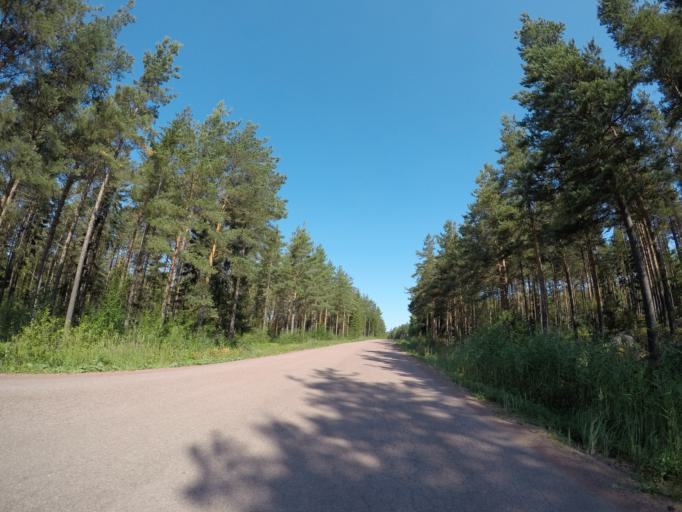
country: AX
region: Alands landsbygd
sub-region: Saltvik
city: Saltvik
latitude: 60.2293
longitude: 20.0079
